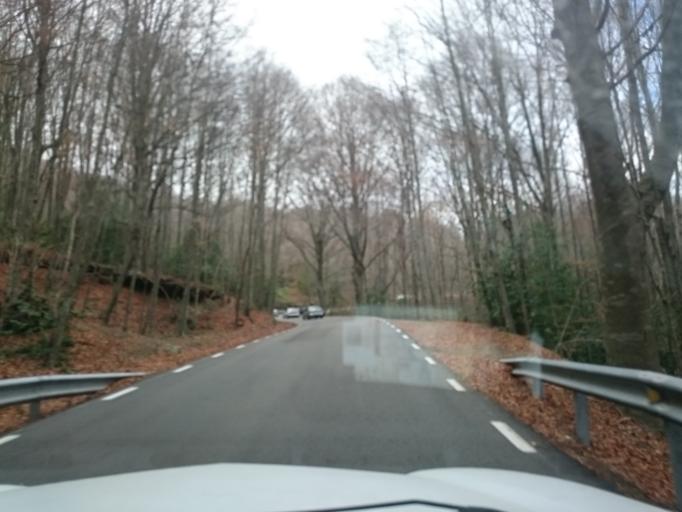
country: ES
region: Catalonia
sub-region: Provincia de Barcelona
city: Fogars de Montclus
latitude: 41.7643
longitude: 2.4676
